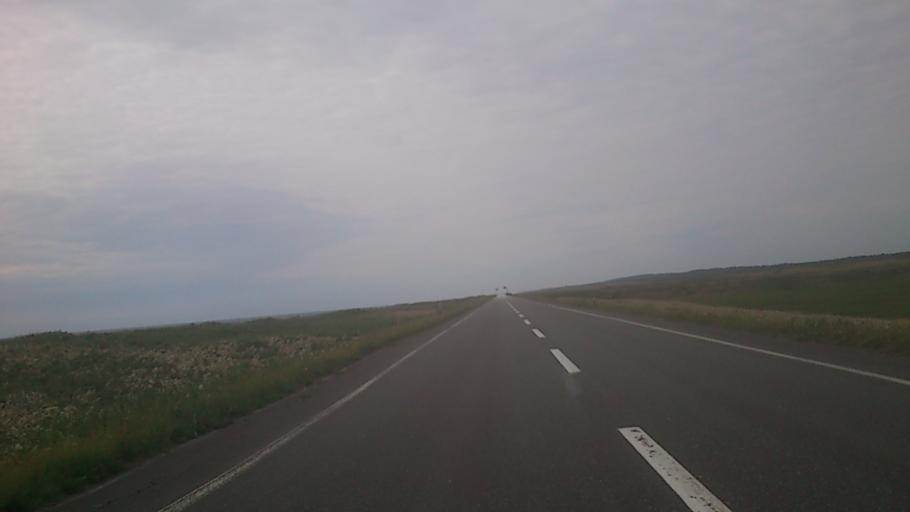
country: JP
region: Hokkaido
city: Makubetsu
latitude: 45.0360
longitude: 141.6616
